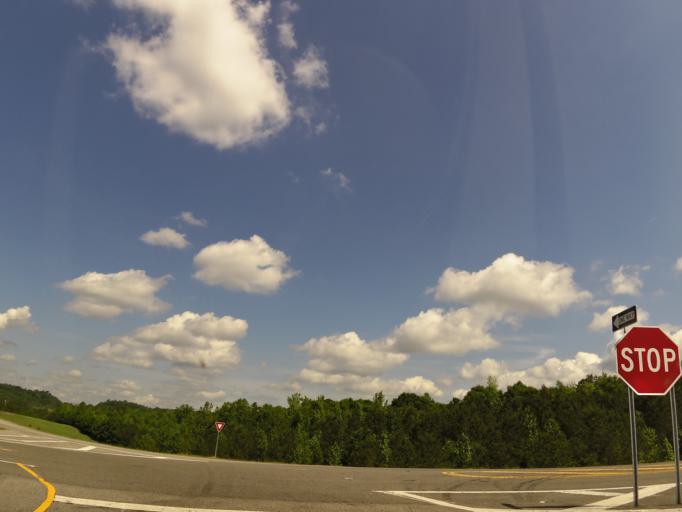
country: US
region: Alabama
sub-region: Marion County
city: Winfield
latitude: 34.0128
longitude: -87.8328
